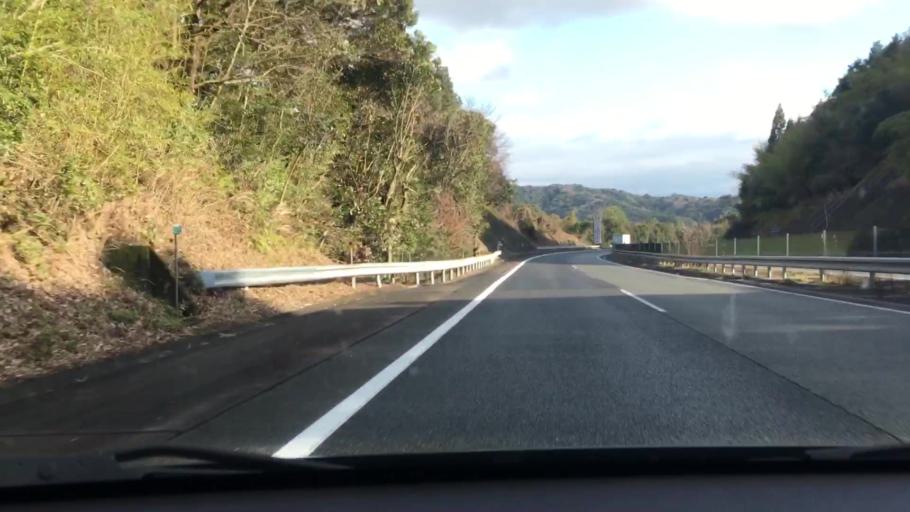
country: JP
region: Kumamoto
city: Hitoyoshi
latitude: 32.2668
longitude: 130.7636
